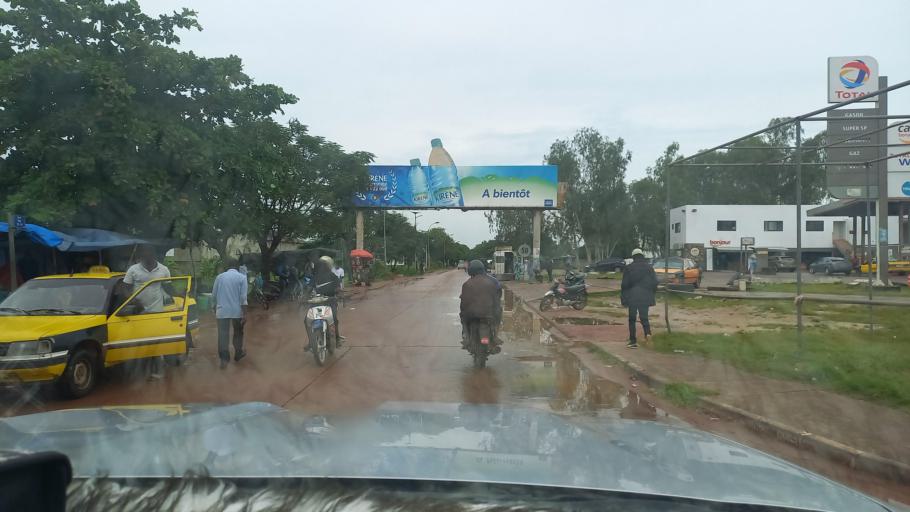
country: SN
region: Ziguinchor
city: Ziguinchor
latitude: 12.5823
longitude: -16.2639
